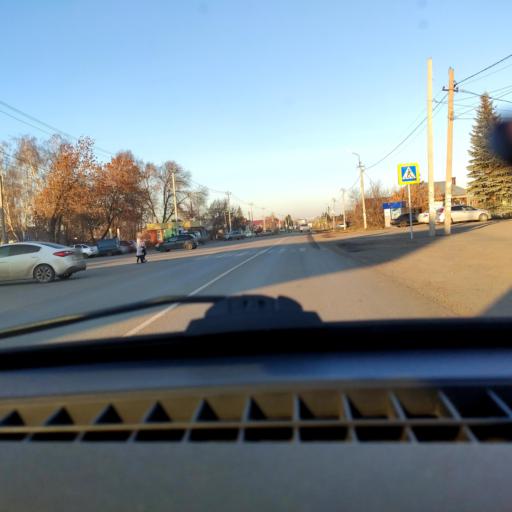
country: RU
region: Bashkortostan
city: Ufa
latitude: 54.6147
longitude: 55.9020
